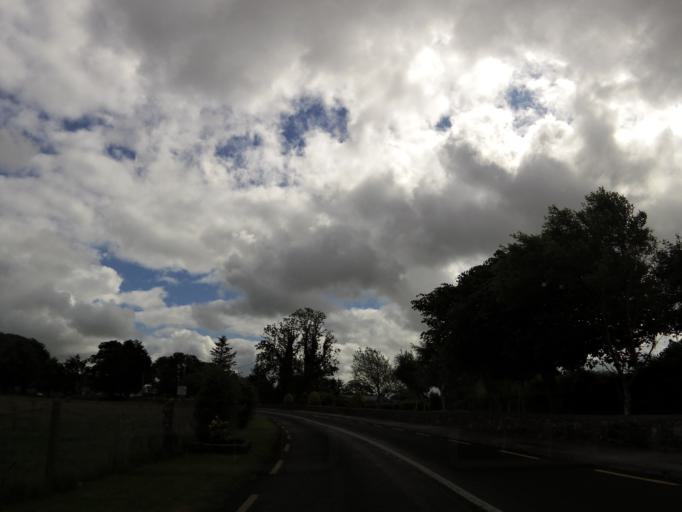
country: IE
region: Connaught
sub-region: County Galway
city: Loughrea
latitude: 53.4283
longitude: -8.4784
